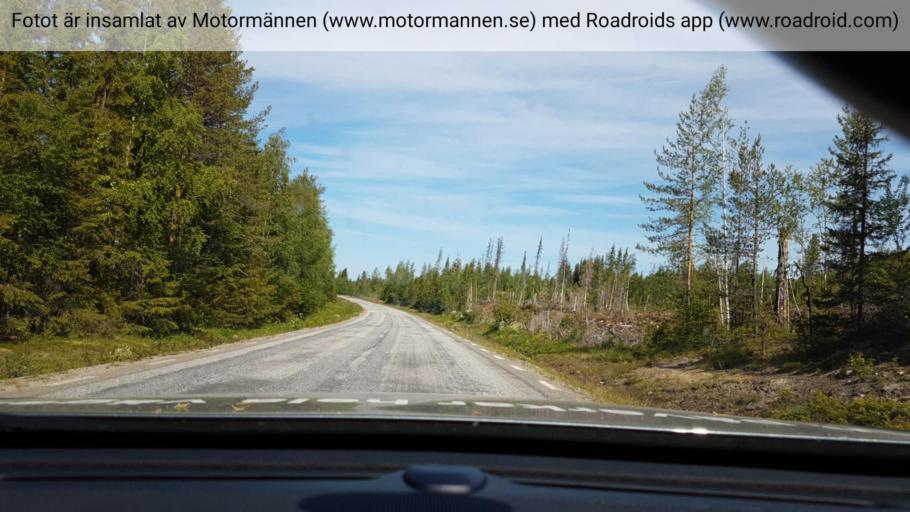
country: SE
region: Vaesterbotten
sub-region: Vilhelmina Kommun
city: Sjoberg
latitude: 64.6020
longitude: 15.8625
